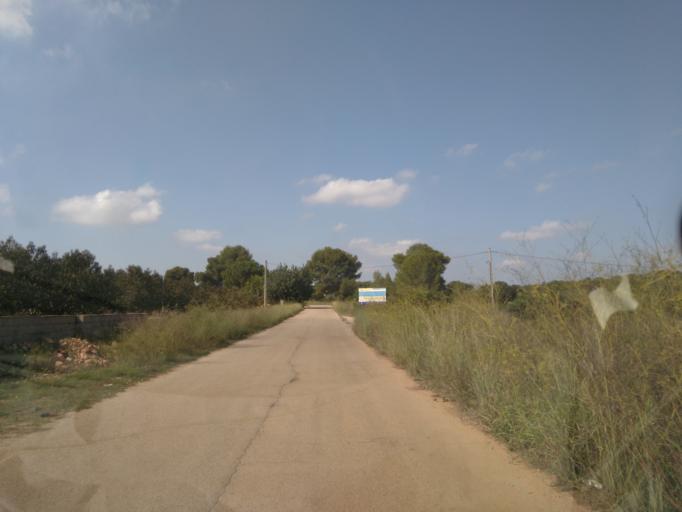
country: ES
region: Valencia
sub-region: Provincia de Valencia
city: Masalaves
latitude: 39.1717
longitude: -0.5559
